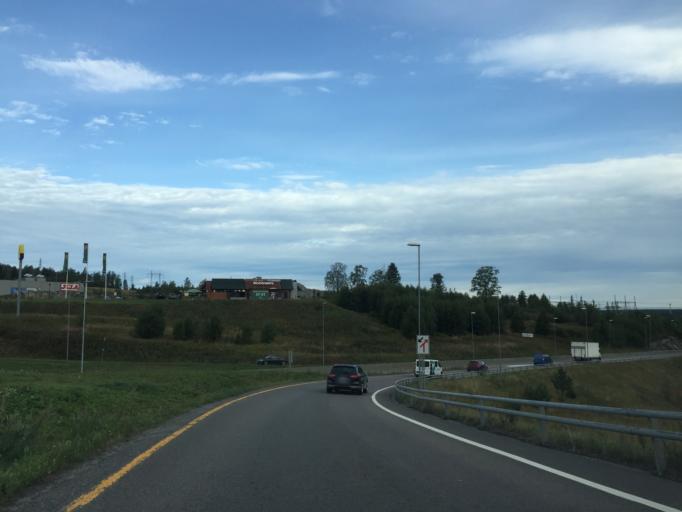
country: NO
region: Akershus
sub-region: Ski
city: Ski
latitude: 59.7250
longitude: 10.7867
